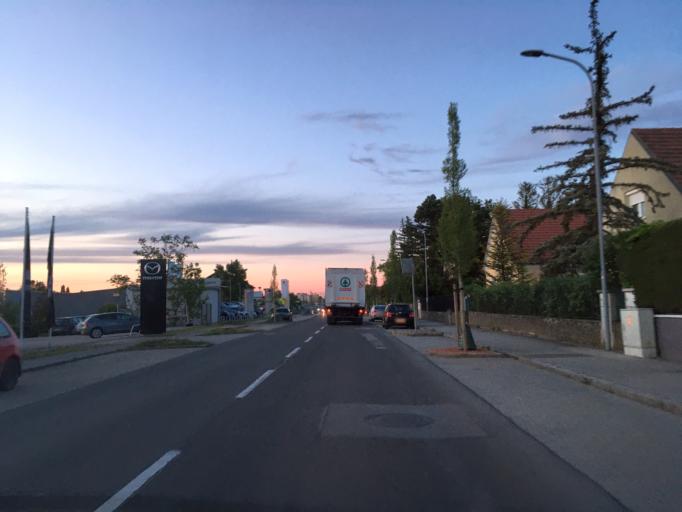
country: AT
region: Lower Austria
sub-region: Politischer Bezirk Wien-Umgebung
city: Zwolfaxing
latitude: 48.1170
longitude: 16.4673
